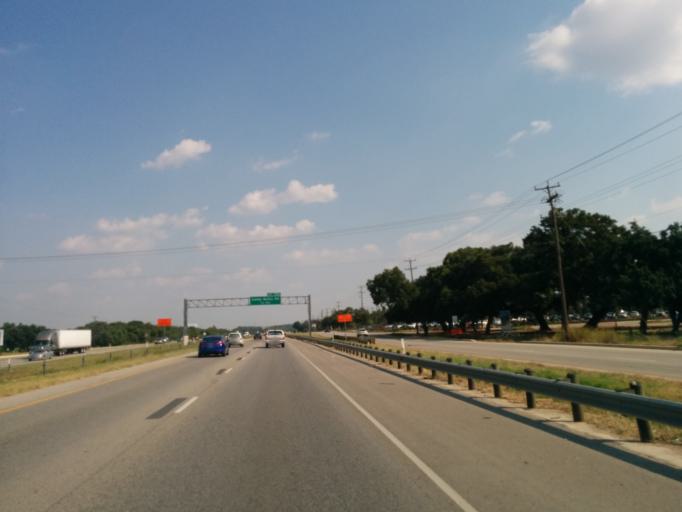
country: US
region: Texas
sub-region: Bexar County
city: Cross Mountain
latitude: 29.6443
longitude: -98.6201
